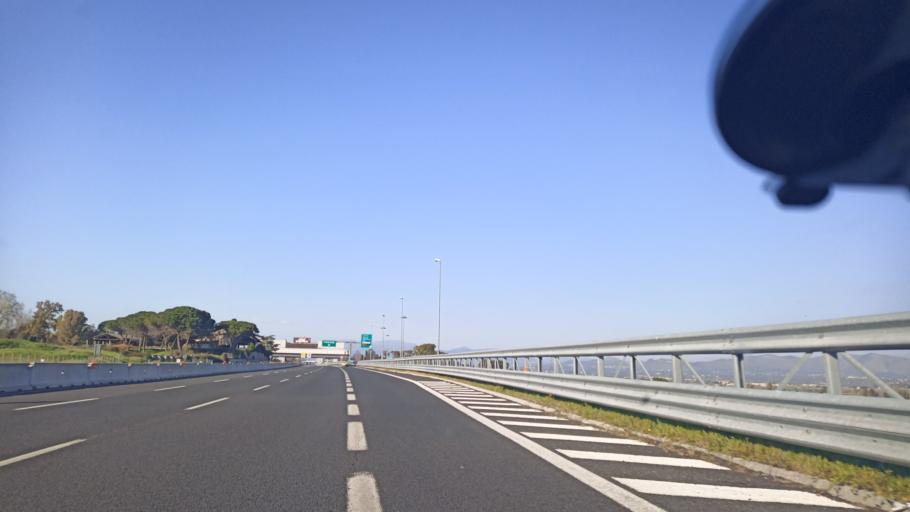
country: IT
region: Latium
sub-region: Citta metropolitana di Roma Capitale
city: Bivio di Capanelle
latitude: 42.1298
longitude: 12.5998
